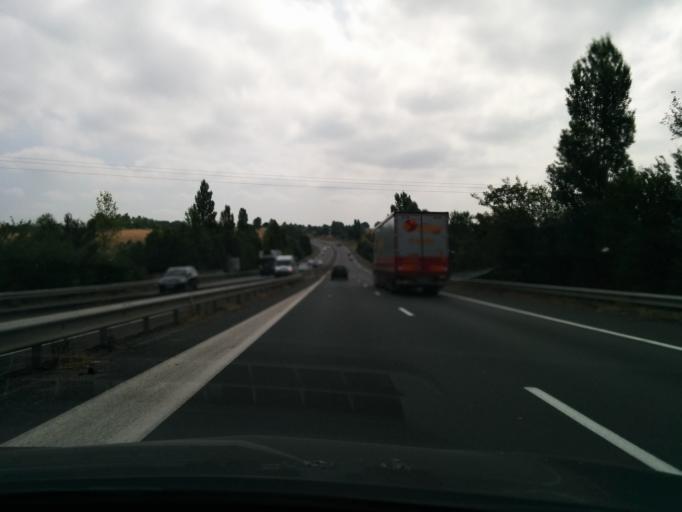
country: FR
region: Midi-Pyrenees
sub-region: Departement de la Haute-Garonne
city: Montrabe
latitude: 43.6547
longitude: 1.5312
